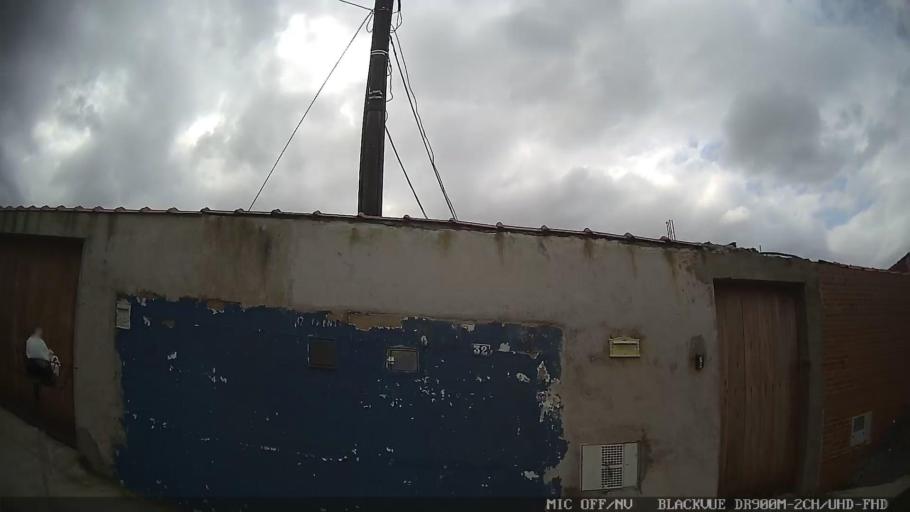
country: BR
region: Sao Paulo
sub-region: Guaruja
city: Guaruja
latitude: -23.9916
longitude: -46.2885
